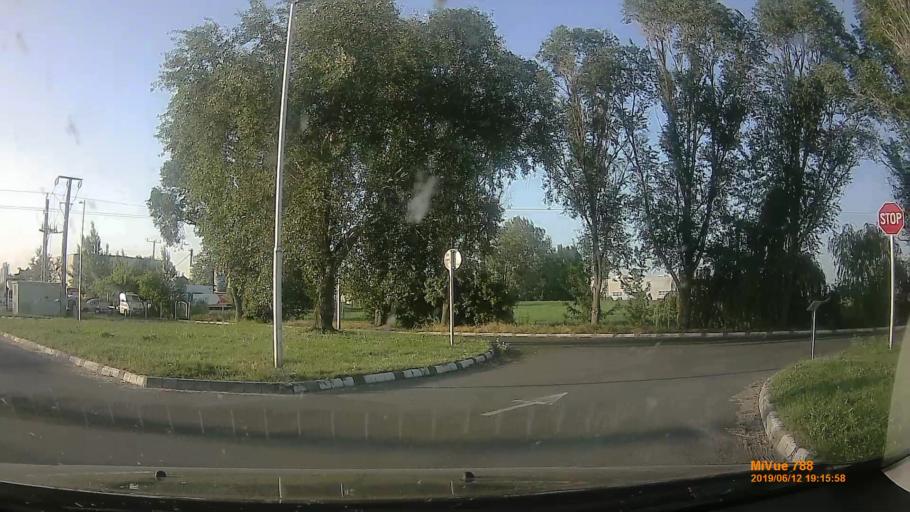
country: HU
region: Bacs-Kiskun
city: Kecskemet
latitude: 46.8823
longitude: 19.7081
